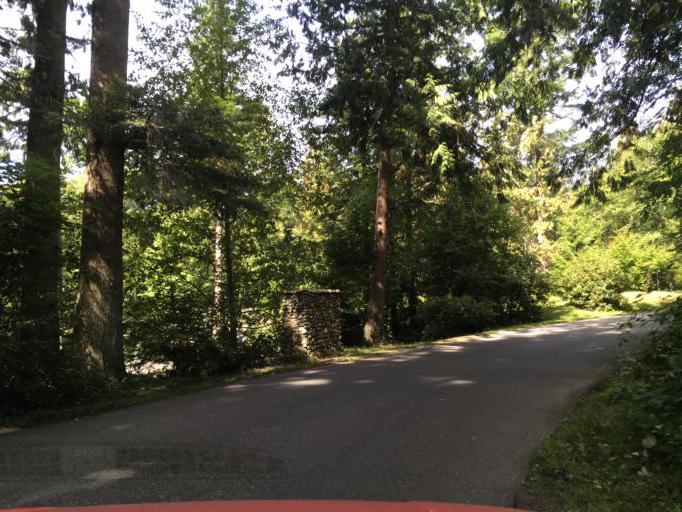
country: US
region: Washington
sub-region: Whatcom County
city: Bellingham
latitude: 48.6531
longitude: -122.4908
